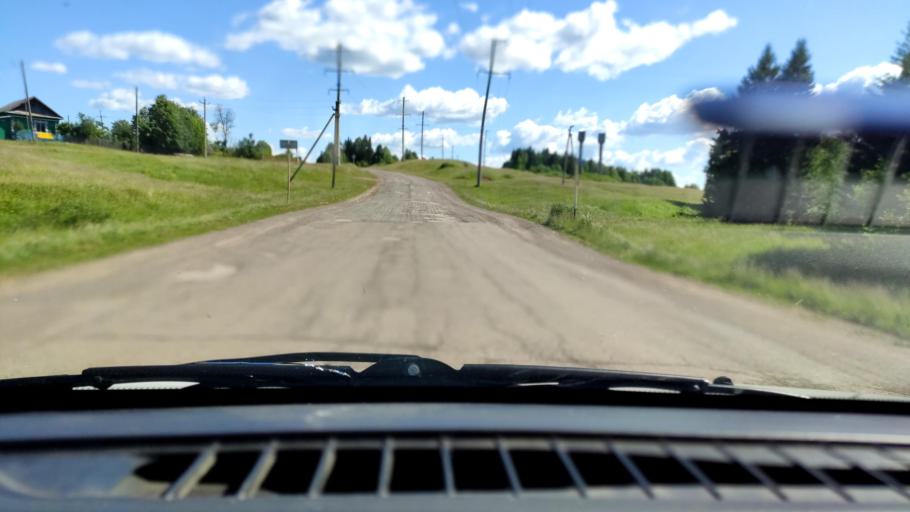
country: RU
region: Perm
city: Uinskoye
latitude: 57.1776
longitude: 56.5598
